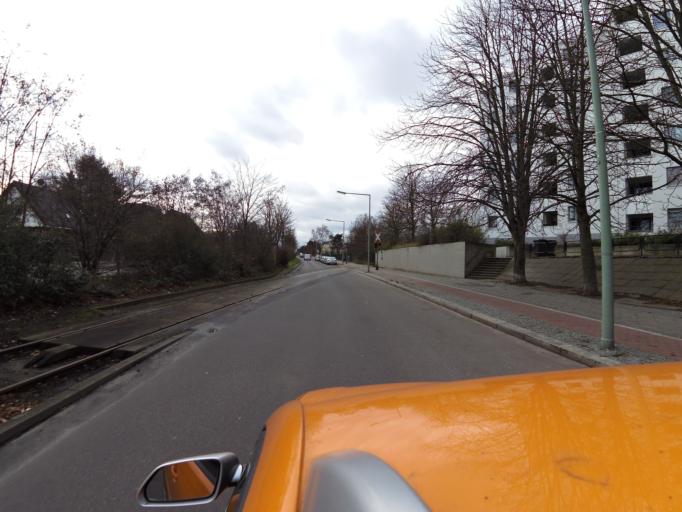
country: DE
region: Berlin
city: Rudow
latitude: 52.4206
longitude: 13.4807
